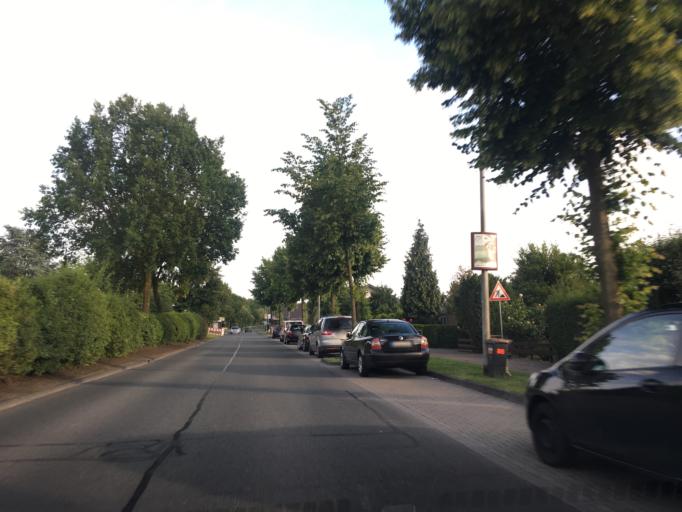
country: DE
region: North Rhine-Westphalia
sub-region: Regierungsbezirk Munster
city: Senden
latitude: 51.9188
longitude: 7.5277
